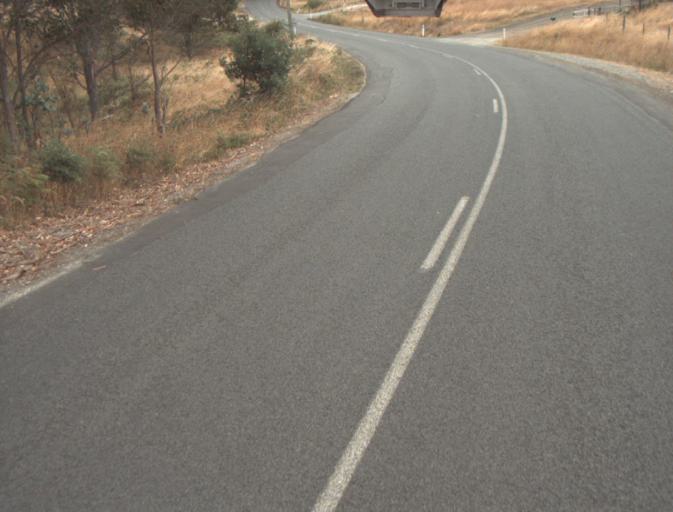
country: AU
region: Tasmania
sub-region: Launceston
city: Mayfield
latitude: -41.1876
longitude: 147.2220
